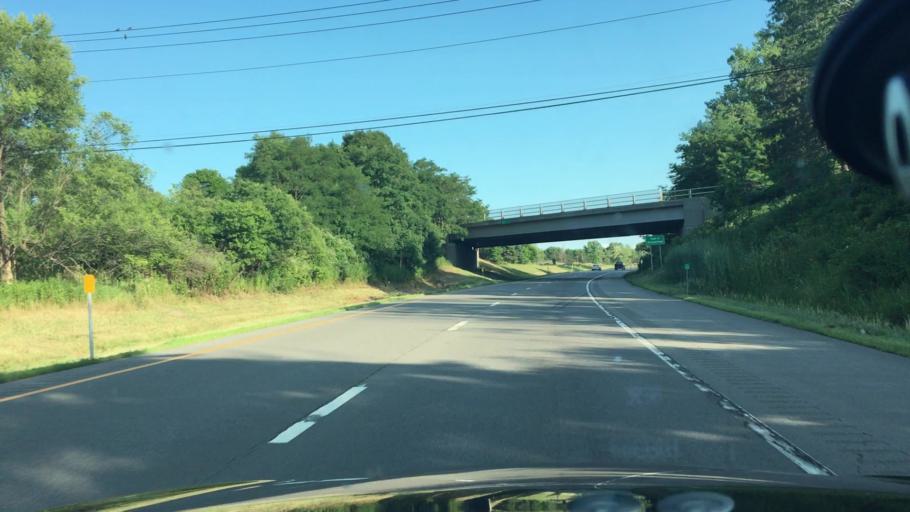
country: US
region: New York
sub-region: Erie County
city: Blasdell
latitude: 42.8048
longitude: -78.7801
